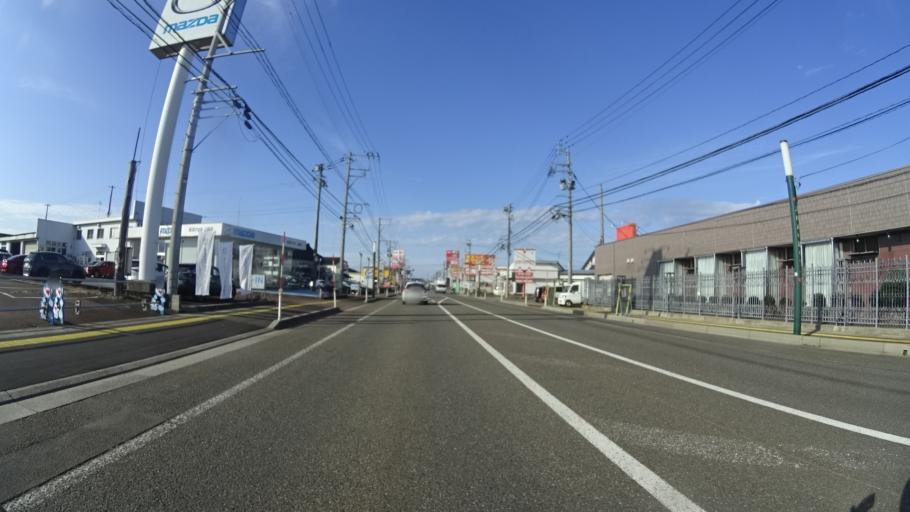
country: JP
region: Niigata
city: Joetsu
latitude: 37.1319
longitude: 138.2446
